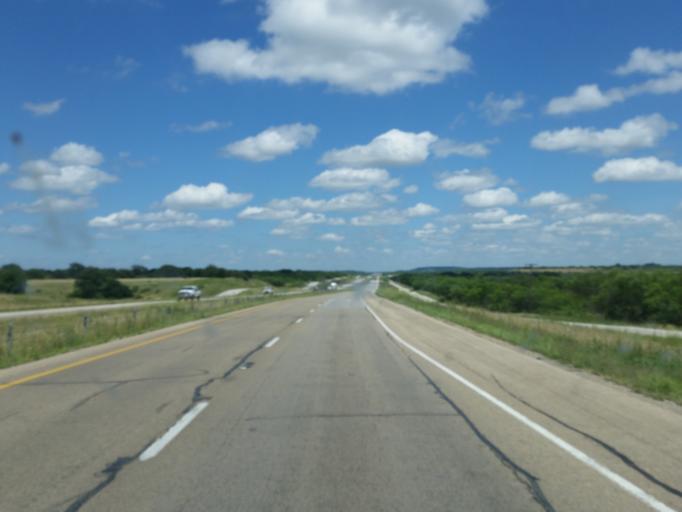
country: US
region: Texas
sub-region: Callahan County
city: Baird
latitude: 32.3850
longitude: -99.2918
